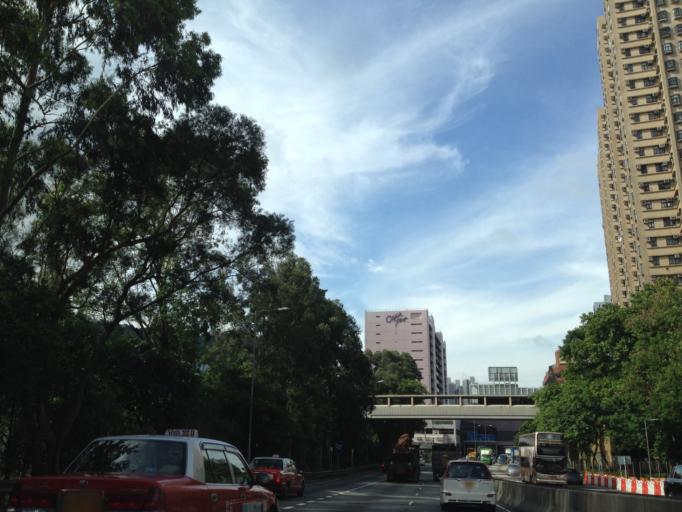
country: HK
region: Sha Tin
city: Sha Tin
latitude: 22.3801
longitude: 114.1861
